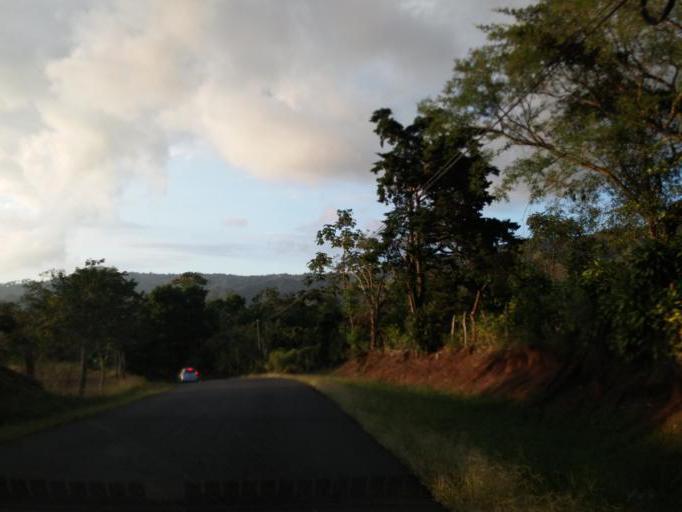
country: CR
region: San Jose
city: Palmichal
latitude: 9.8456
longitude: -84.2184
